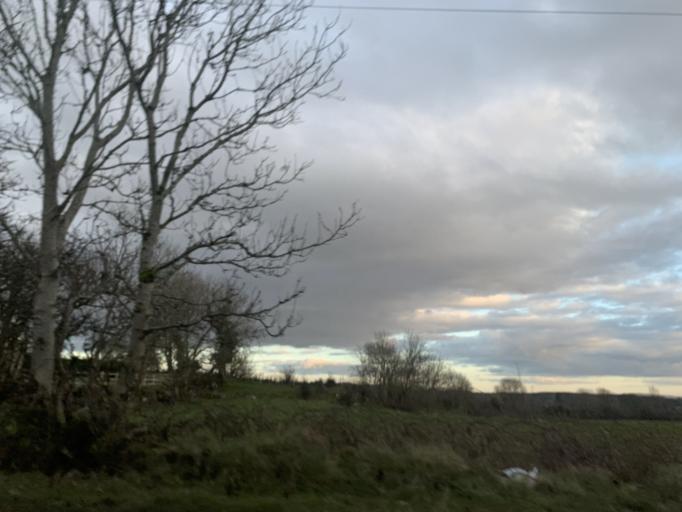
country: IE
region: Connaught
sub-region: Sligo
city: Tobercurry
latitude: 54.0638
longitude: -8.7120
